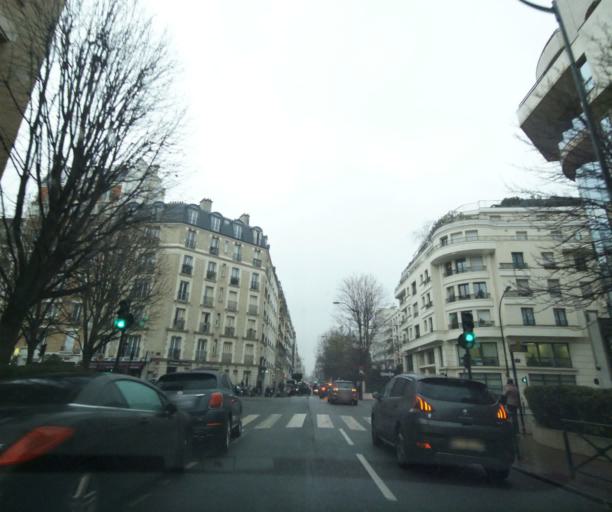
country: FR
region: Ile-de-France
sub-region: Departement des Hauts-de-Seine
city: Levallois-Perret
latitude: 48.8940
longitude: 2.2833
